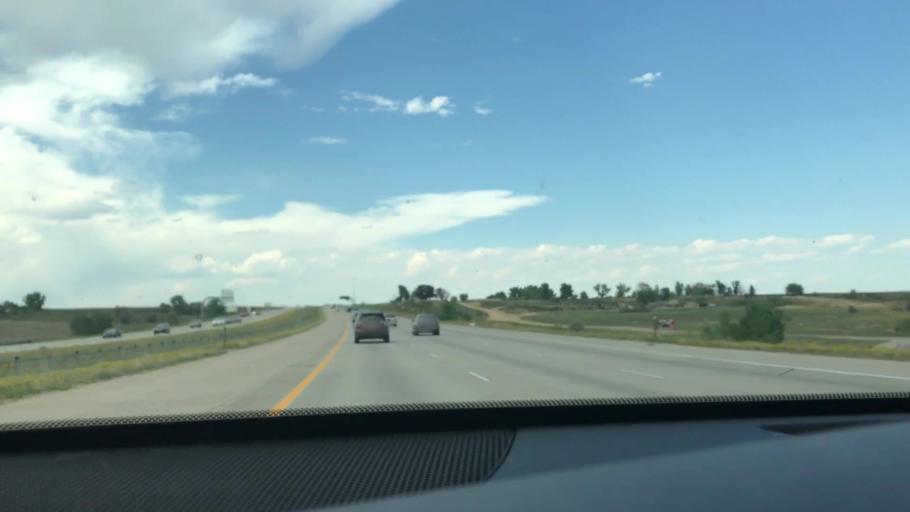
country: US
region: Colorado
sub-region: Weld County
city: Mead
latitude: 40.1781
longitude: -104.9791
